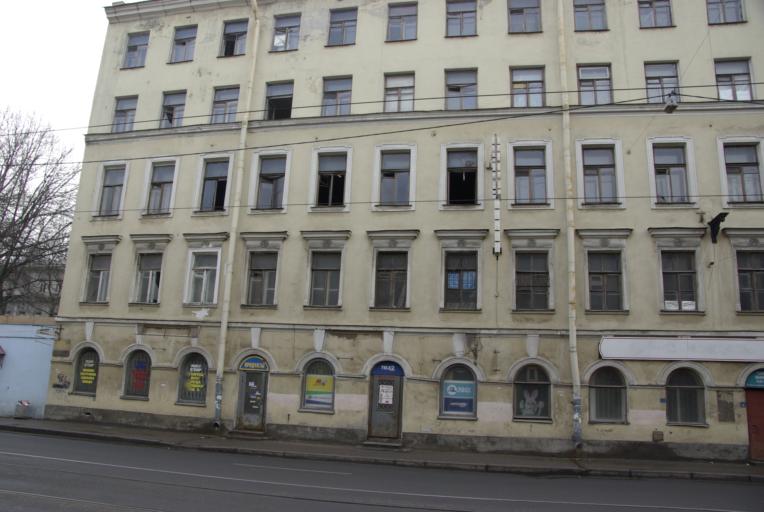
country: RU
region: St.-Petersburg
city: Admiralteisky
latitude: 59.9100
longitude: 30.2756
